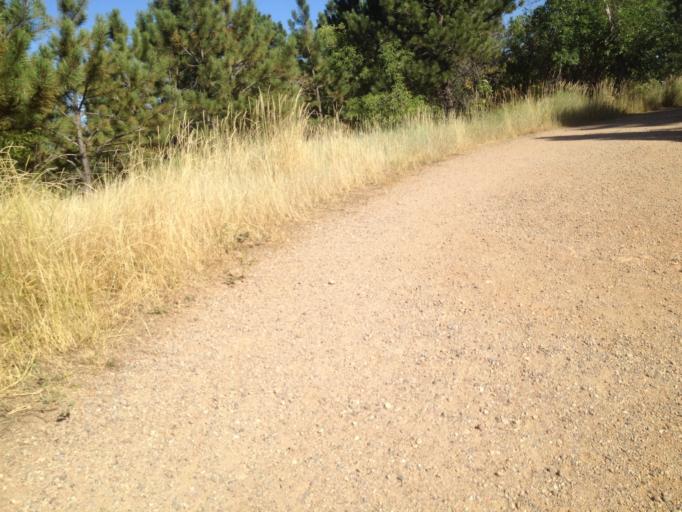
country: US
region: Colorado
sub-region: Boulder County
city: Boulder
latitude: 39.9957
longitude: -105.2787
